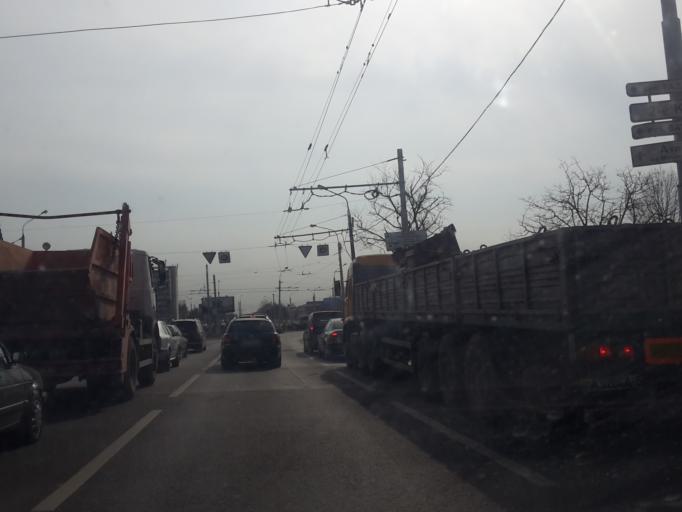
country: BY
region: Minsk
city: Minsk
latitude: 53.8957
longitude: 27.6428
